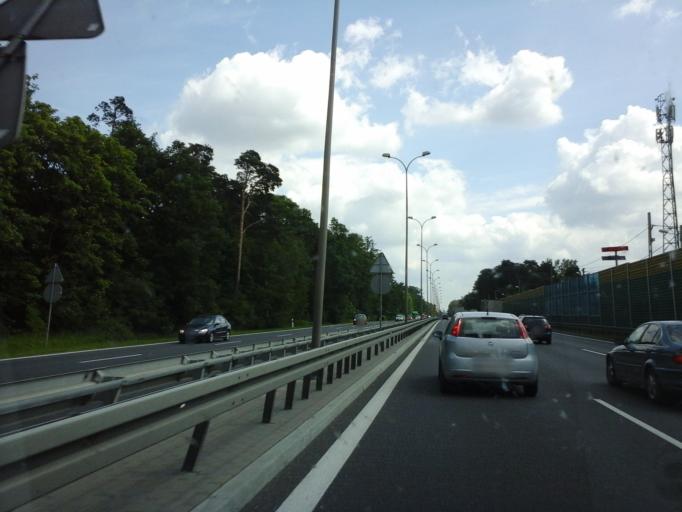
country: PL
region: Lodz Voivodeship
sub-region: Powiat lodzki wschodni
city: Tuszyn
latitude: 51.6209
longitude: 19.5178
